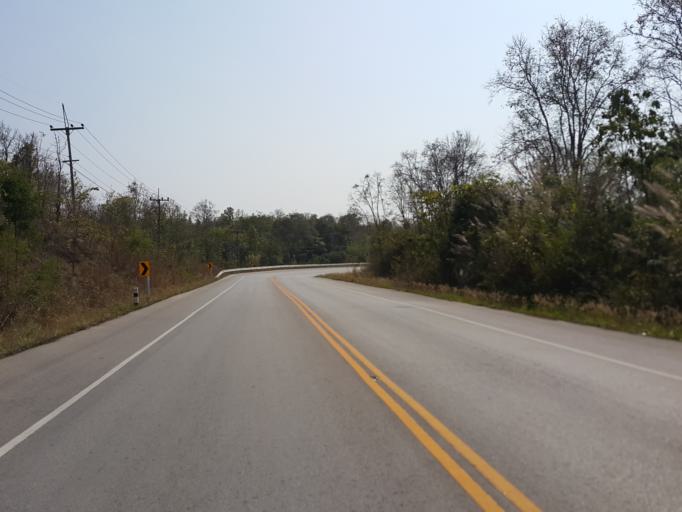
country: TH
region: Lampang
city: Wang Nuea
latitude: 18.9479
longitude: 99.6120
